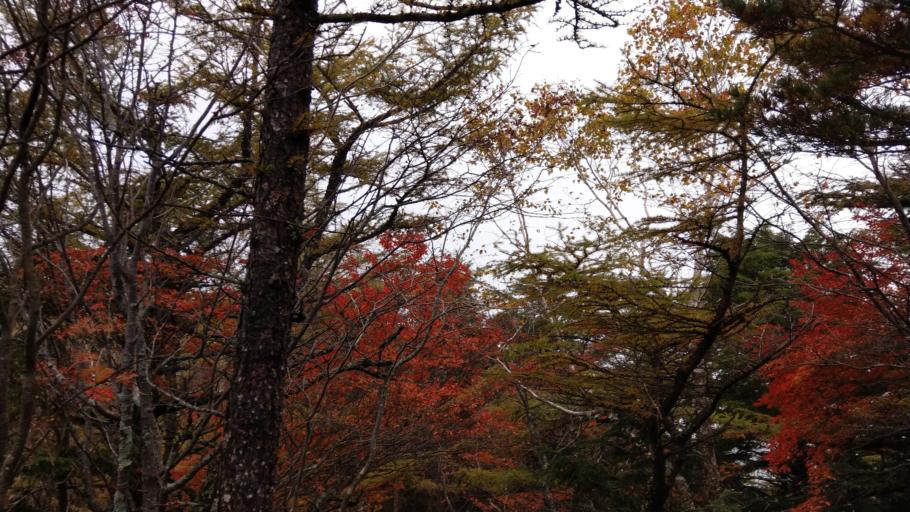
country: JP
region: Nagano
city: Komoro
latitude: 36.4037
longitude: 138.4589
